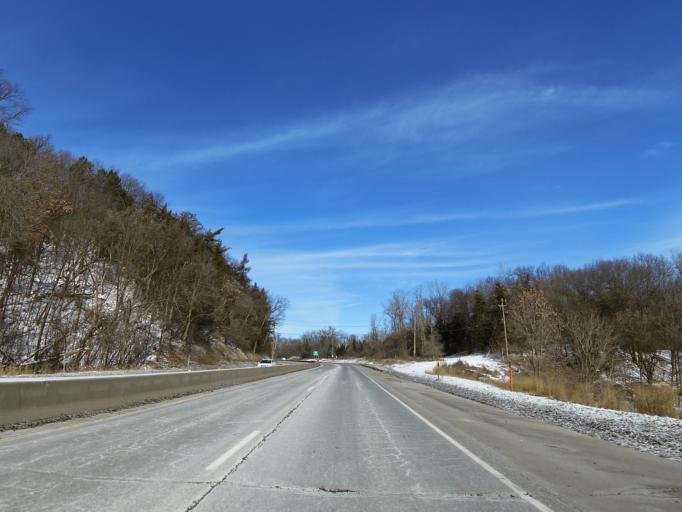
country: US
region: Minnesota
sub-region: Dakota County
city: Hastings
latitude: 44.7593
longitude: -92.8535
